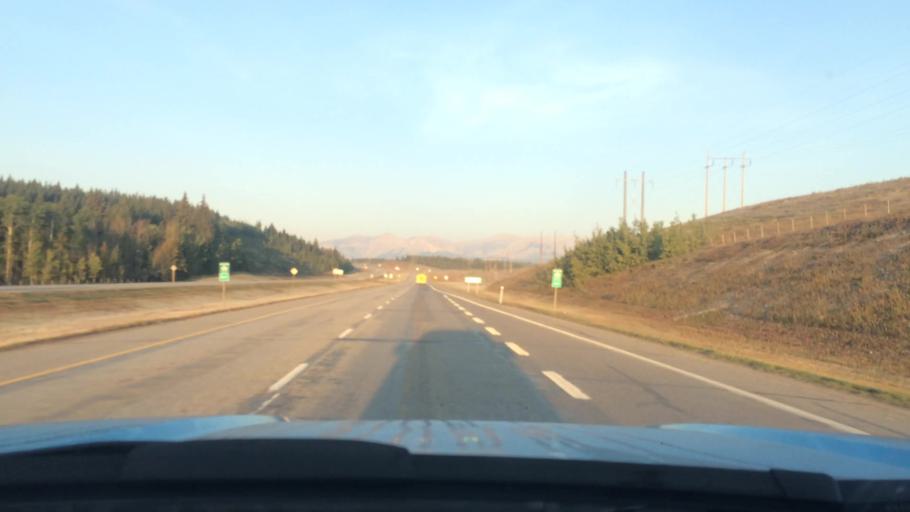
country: CA
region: Alberta
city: Cochrane
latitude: 51.1471
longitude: -114.8524
